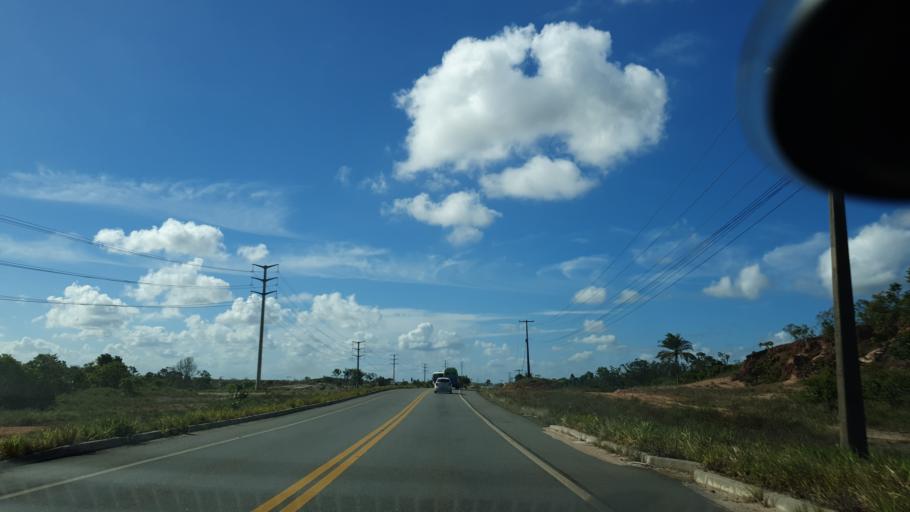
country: BR
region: Bahia
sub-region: Camacari
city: Camacari
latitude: -12.6986
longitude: -38.2186
